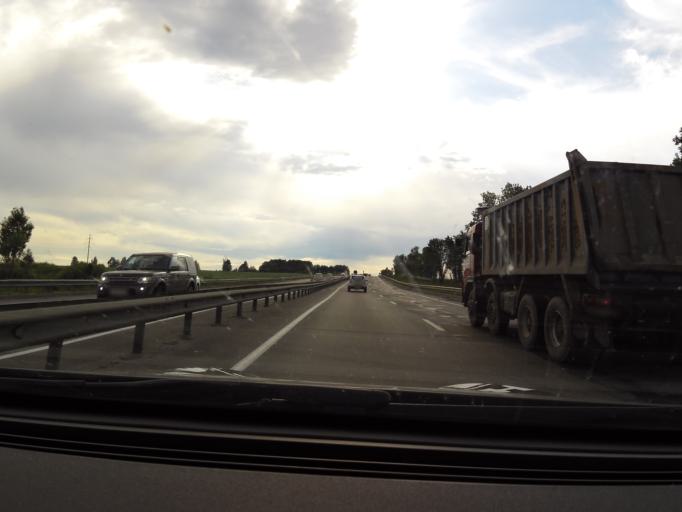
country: RU
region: Vladimir
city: Novovyazniki
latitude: 56.2171
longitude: 42.2303
